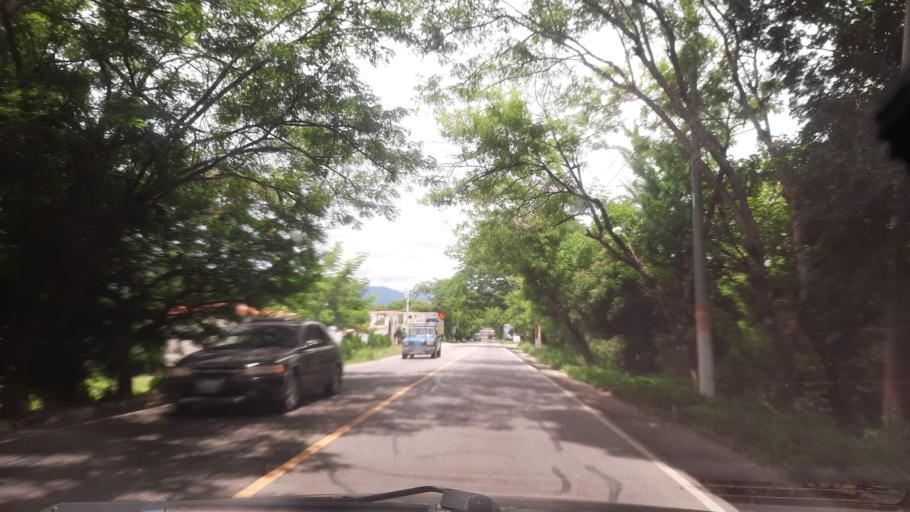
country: GT
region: Zacapa
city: Estanzuela
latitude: 14.9851
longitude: -89.5607
